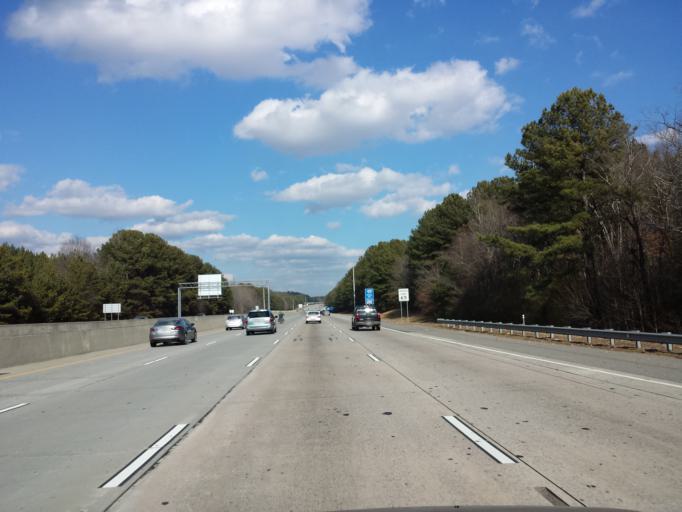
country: US
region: Georgia
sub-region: Fulton County
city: Alpharetta
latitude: 34.0942
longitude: -84.2551
